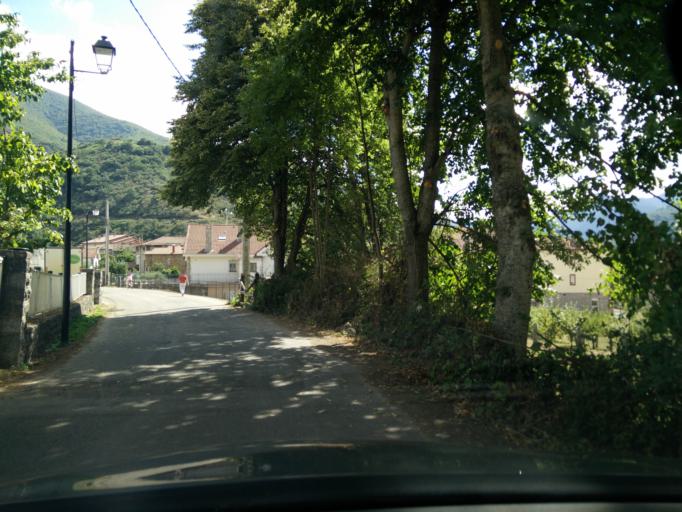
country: ES
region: Castille and Leon
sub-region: Provincia de Leon
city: Posada de Valdeon
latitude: 43.1526
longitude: -4.9163
